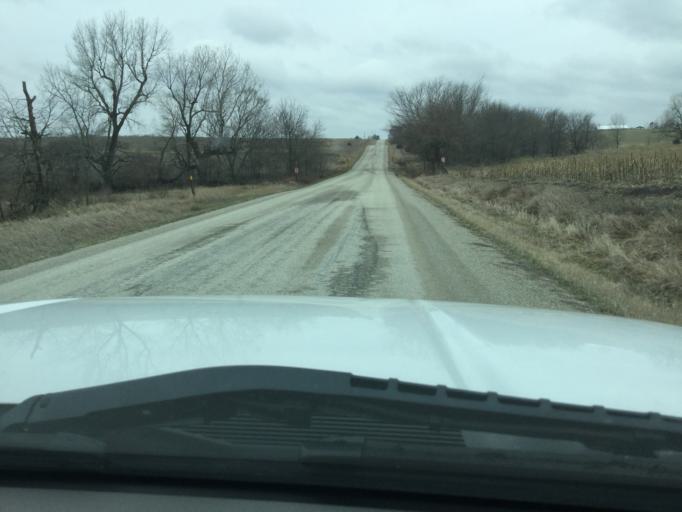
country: US
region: Kansas
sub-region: Nemaha County
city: Sabetha
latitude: 39.7979
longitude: -95.7468
